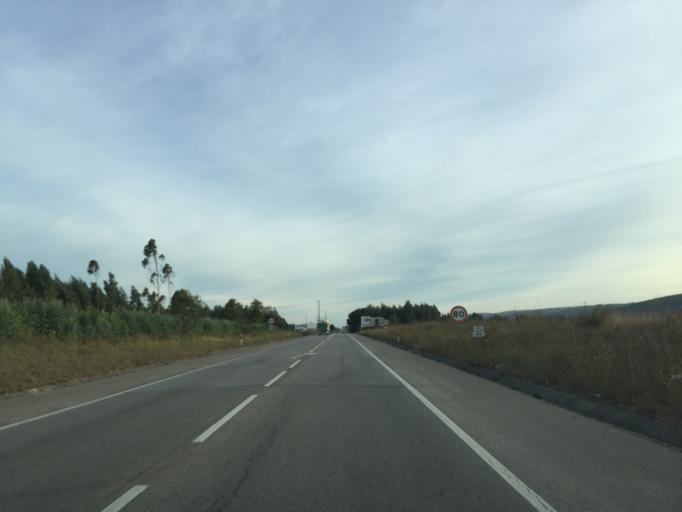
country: PT
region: Leiria
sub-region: Alcobaca
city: Benedita
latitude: 39.4213
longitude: -8.9621
